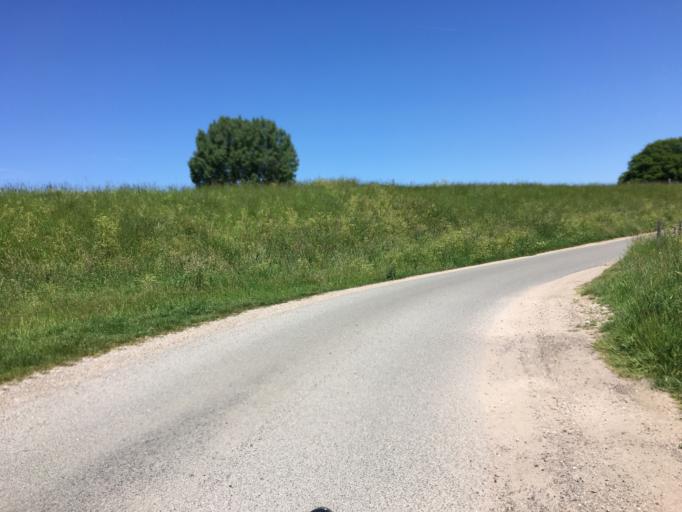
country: NL
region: North Brabant
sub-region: Gemeente Heusden
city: Heusden
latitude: 51.7406
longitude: 5.1605
